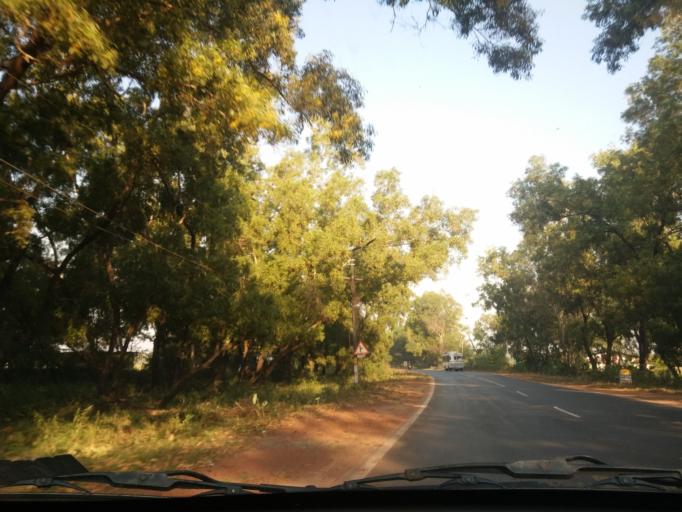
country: IN
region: Goa
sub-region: South Goa
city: Chinchinim
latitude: 15.2088
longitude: 73.9913
